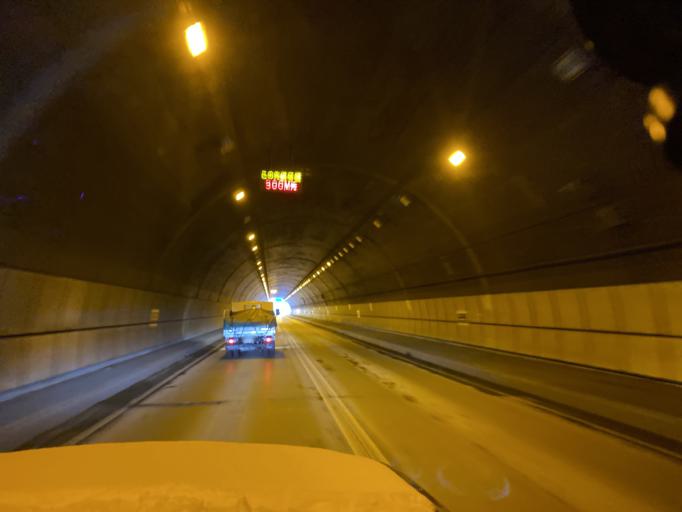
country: JP
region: Nagano
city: Nagano-shi
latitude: 36.6181
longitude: 138.1269
